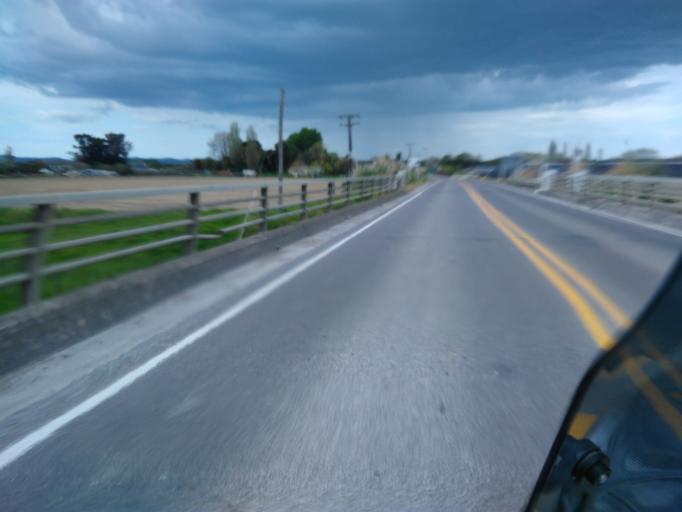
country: NZ
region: Gisborne
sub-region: Gisborne District
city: Gisborne
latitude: -38.6543
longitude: 177.9190
